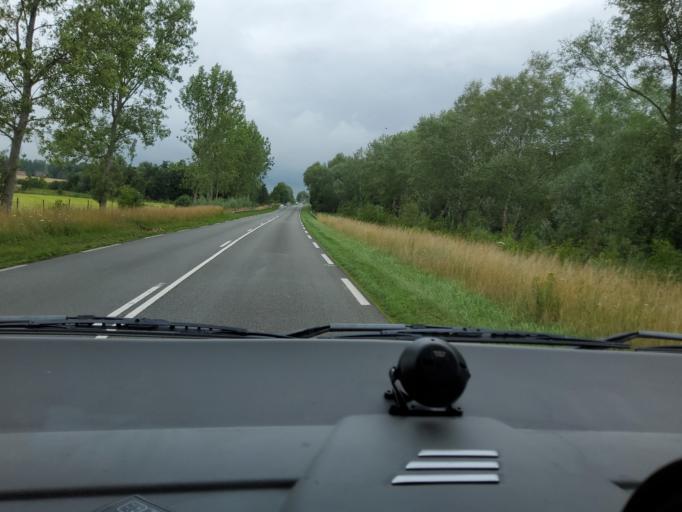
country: FR
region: Nord-Pas-de-Calais
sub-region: Departement du Pas-de-Calais
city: Serques
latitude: 50.8144
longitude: 2.1936
